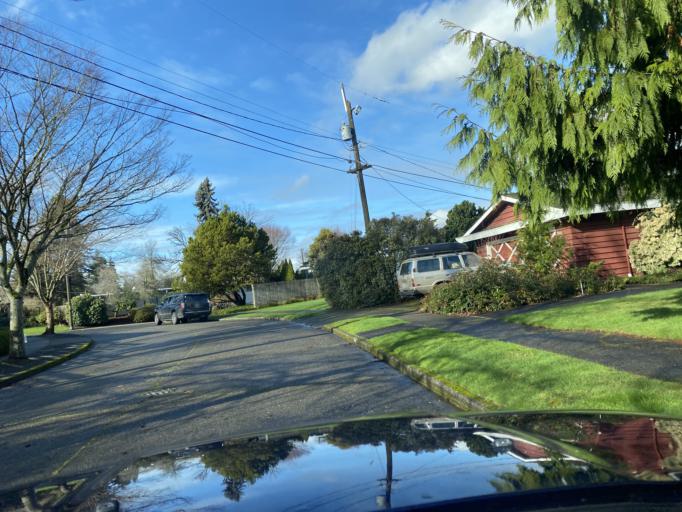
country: US
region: Washington
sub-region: King County
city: Seattle
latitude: 47.6403
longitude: -122.2841
